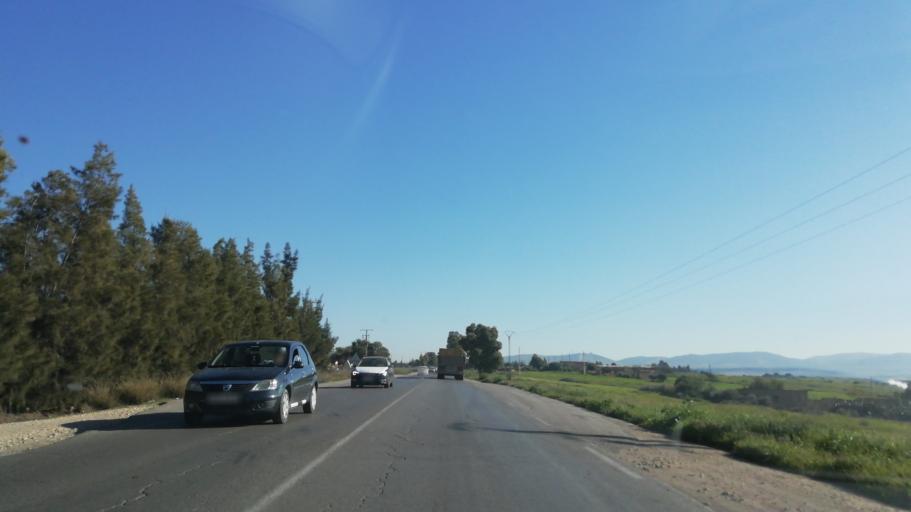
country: DZ
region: Relizane
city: Zemoura
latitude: 35.7504
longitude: 0.6886
